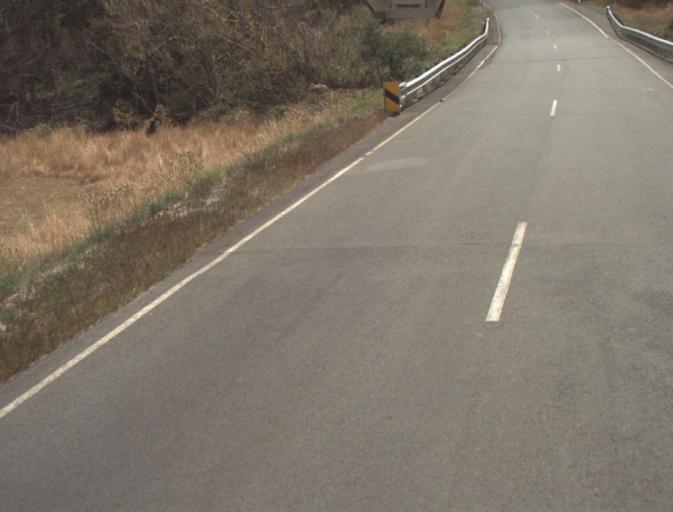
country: AU
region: Tasmania
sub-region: Launceston
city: Mayfield
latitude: -41.2200
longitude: 147.1375
